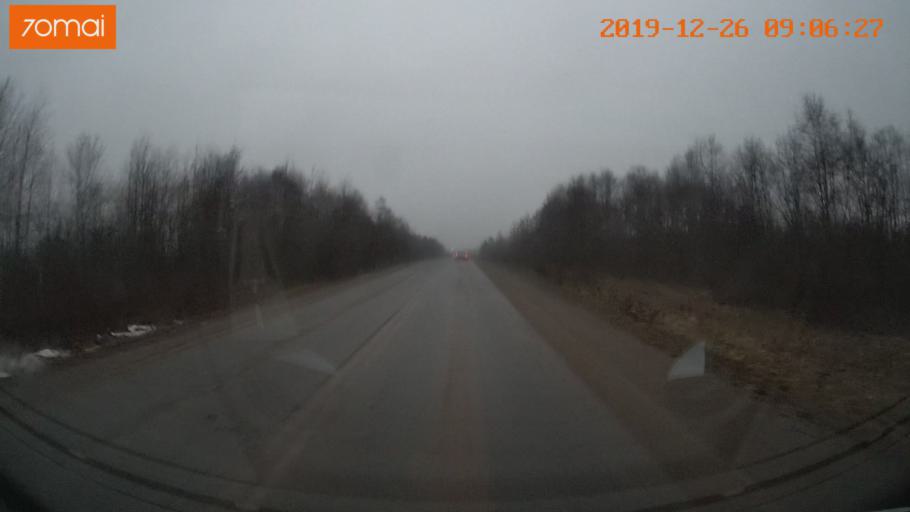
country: RU
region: Vologda
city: Gryazovets
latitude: 58.8360
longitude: 40.2530
